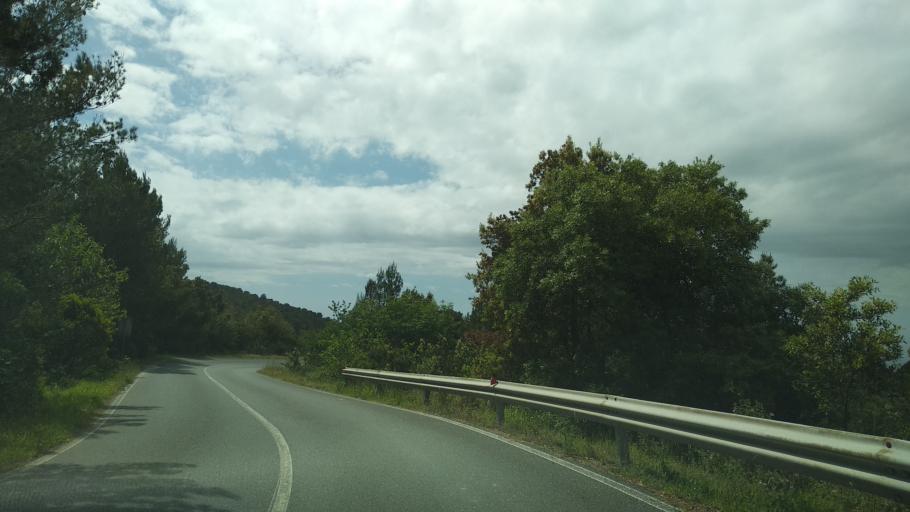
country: IT
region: Tuscany
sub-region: Provincia di Livorno
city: Quercianella
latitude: 43.4948
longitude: 10.3610
